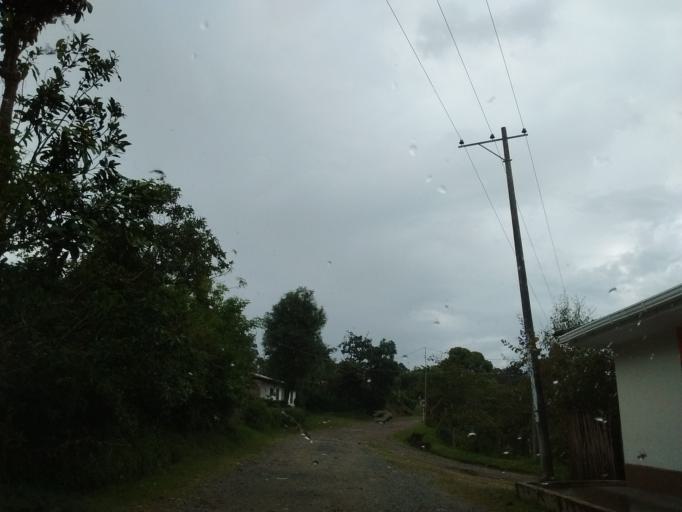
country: CO
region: Cauca
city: Cajibio
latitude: 2.5758
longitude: -76.6550
